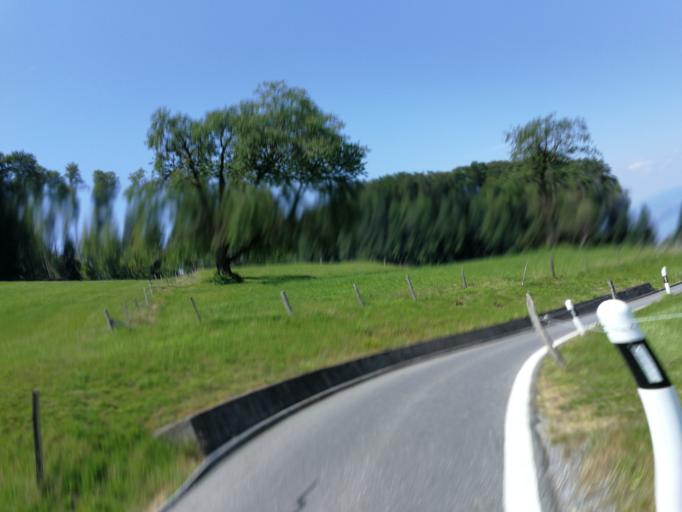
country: CH
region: Schwyz
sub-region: Bezirk Hoefe
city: Freienbach
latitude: 47.1898
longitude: 8.7776
